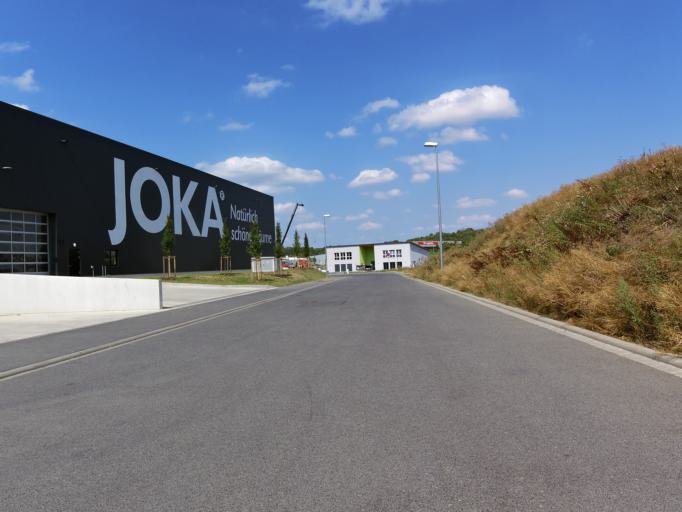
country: DE
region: Bavaria
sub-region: Regierungsbezirk Unterfranken
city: Estenfeld
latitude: 49.8385
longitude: 10.0129
